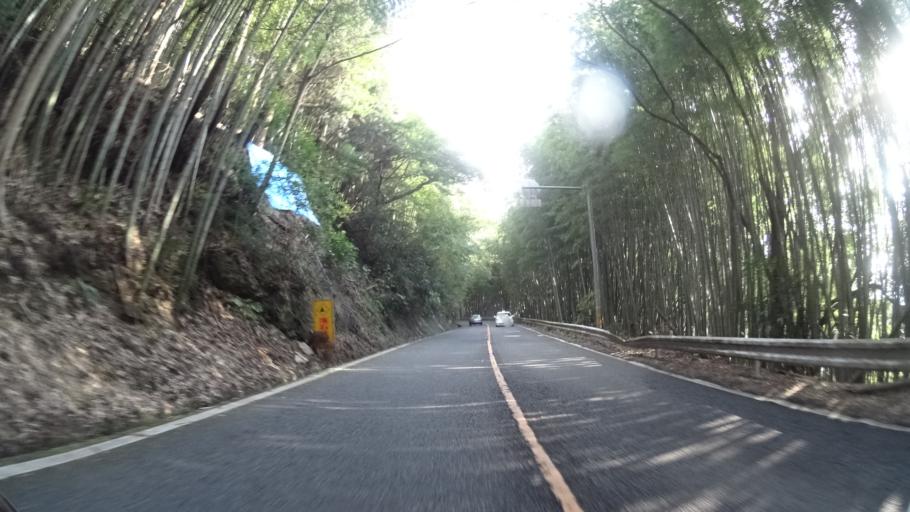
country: JP
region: Oita
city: Beppu
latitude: 33.2686
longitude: 131.3696
